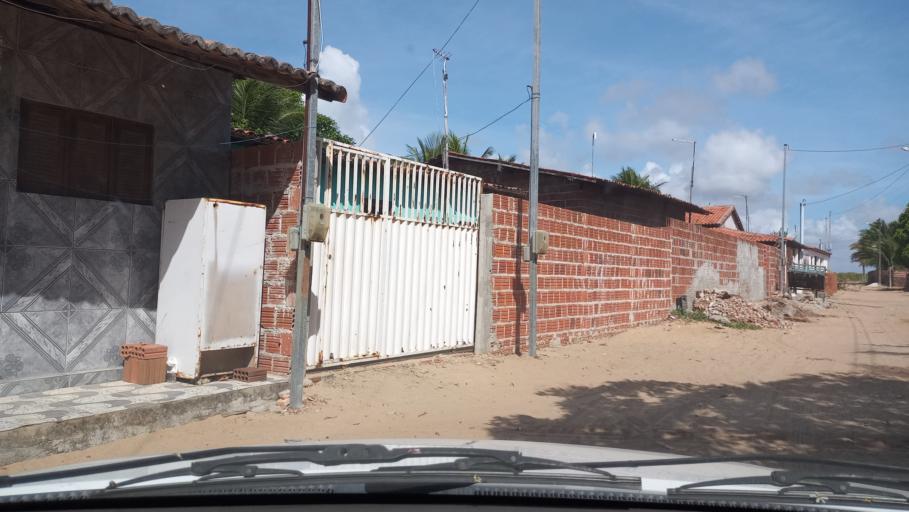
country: BR
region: Rio Grande do Norte
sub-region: Maxaranguape
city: Sao Miguel
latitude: -5.5145
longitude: -35.2651
